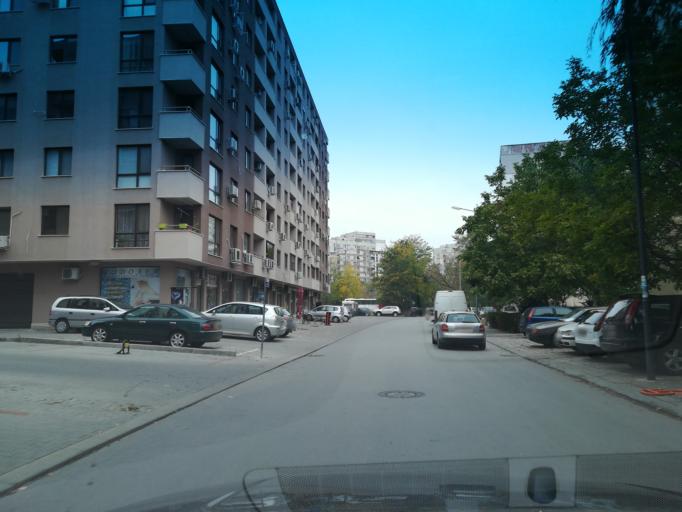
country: BG
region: Plovdiv
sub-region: Obshtina Plovdiv
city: Plovdiv
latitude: 42.1378
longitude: 24.7932
